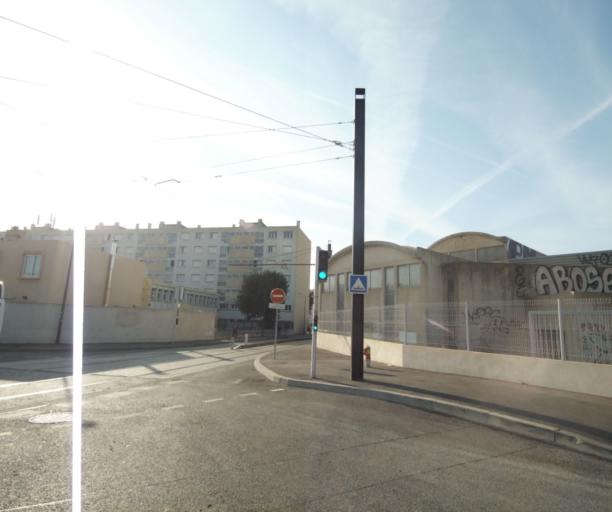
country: FR
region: Provence-Alpes-Cote d'Azur
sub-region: Departement des Bouches-du-Rhone
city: Aubagne
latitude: 43.2955
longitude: 5.5641
